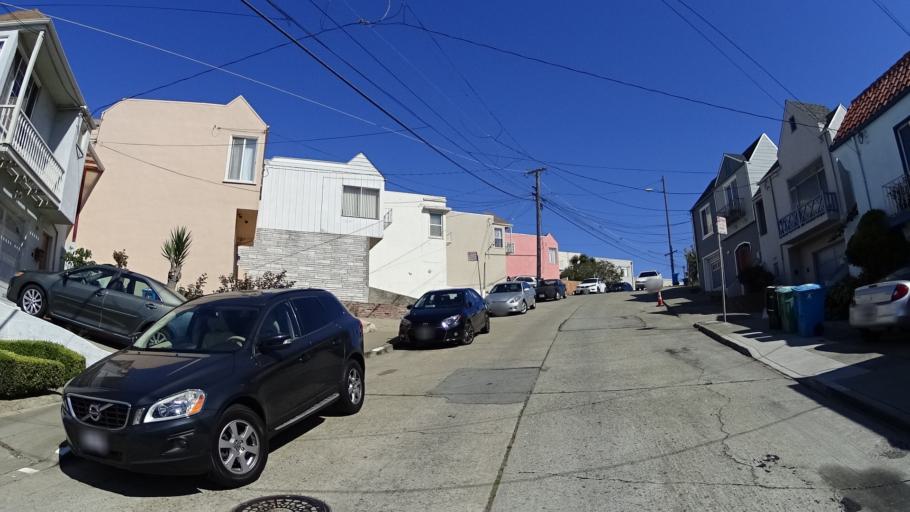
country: US
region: California
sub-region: San Francisco County
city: San Francisco
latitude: 37.7318
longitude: -122.3970
